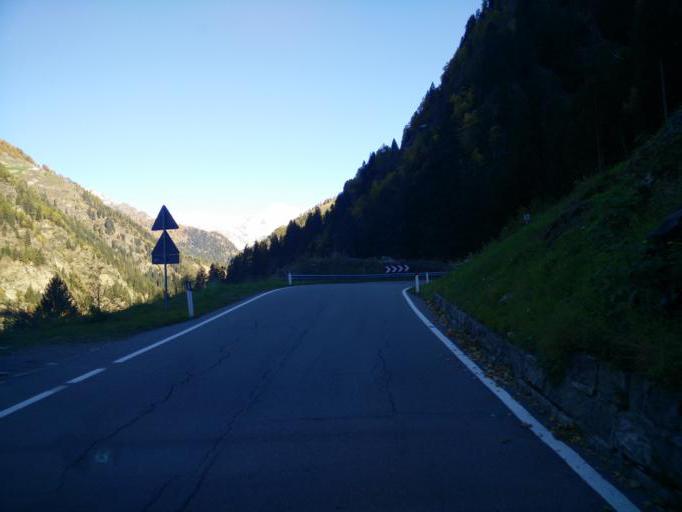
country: IT
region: Trentino-Alto Adige
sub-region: Bolzano
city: Moso in Passiria
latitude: 46.8357
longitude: 11.1681
